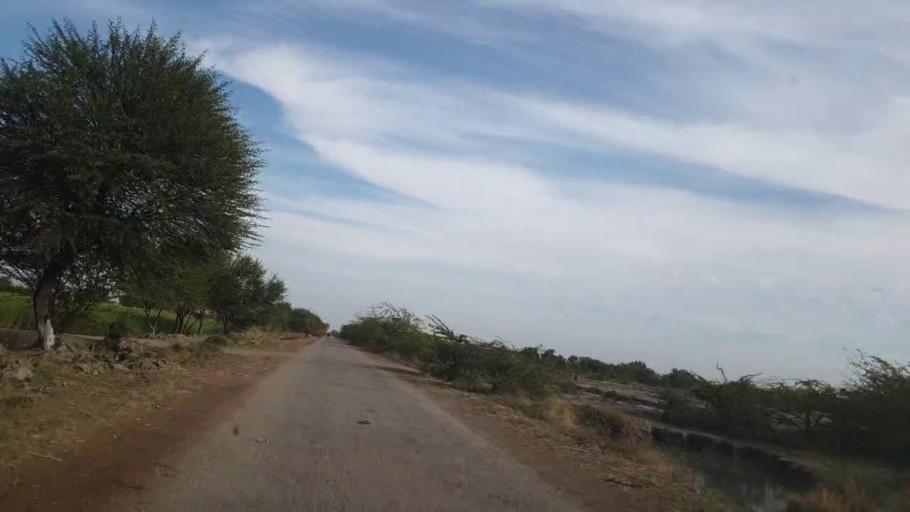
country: PK
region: Sindh
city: Pithoro
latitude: 25.6315
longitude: 69.4041
